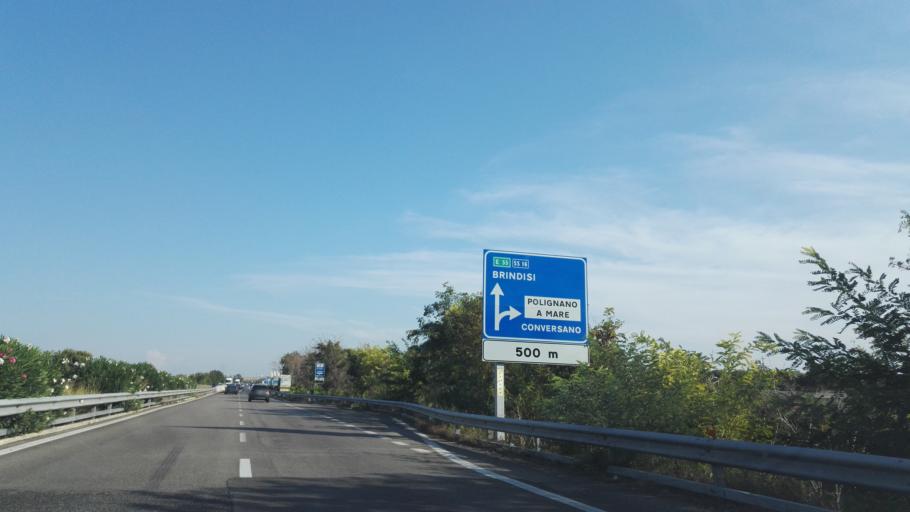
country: IT
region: Apulia
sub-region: Provincia di Bari
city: Polignano a Mare
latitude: 40.9981
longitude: 17.2019
